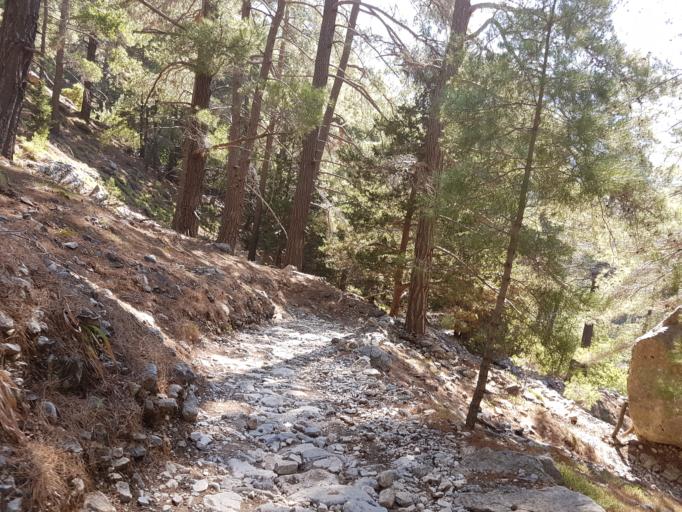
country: GR
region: Crete
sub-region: Nomos Chanias
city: Perivolia
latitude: 35.3064
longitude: 23.9274
